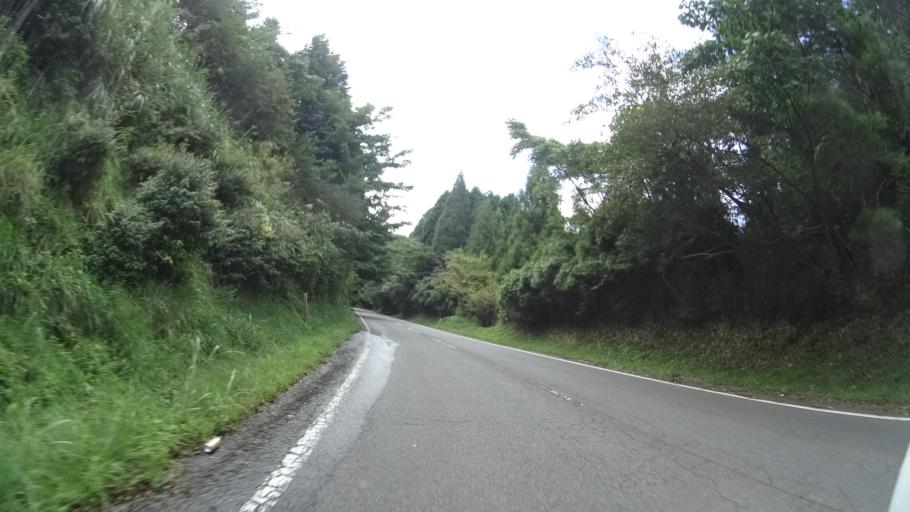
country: JP
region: Oita
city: Beppu
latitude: 33.3262
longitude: 131.4173
